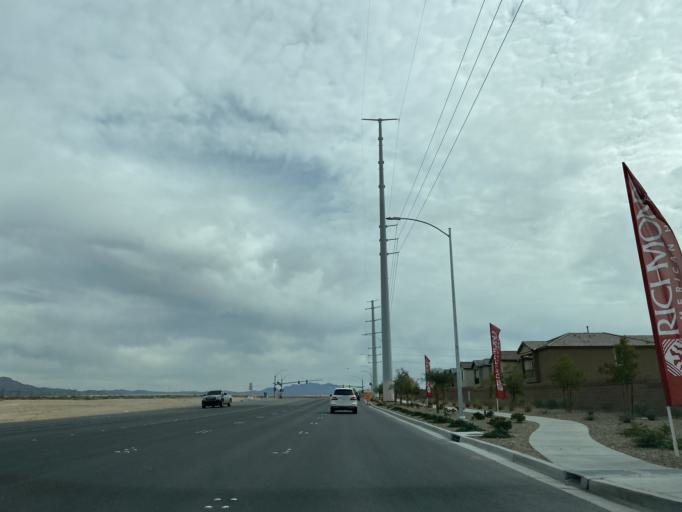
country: US
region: Nevada
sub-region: Clark County
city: Nellis Air Force Base
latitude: 36.2766
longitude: -115.0829
